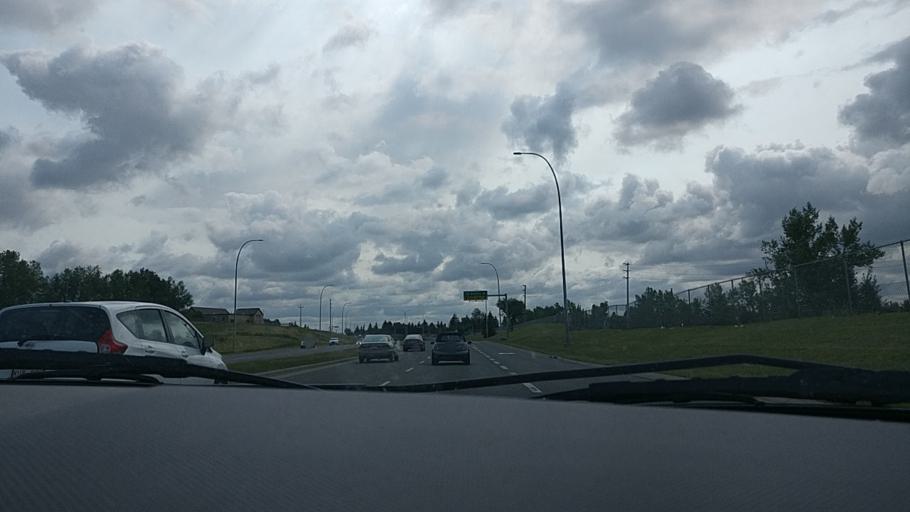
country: CA
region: Alberta
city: Calgary
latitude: 51.0912
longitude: -114.1009
